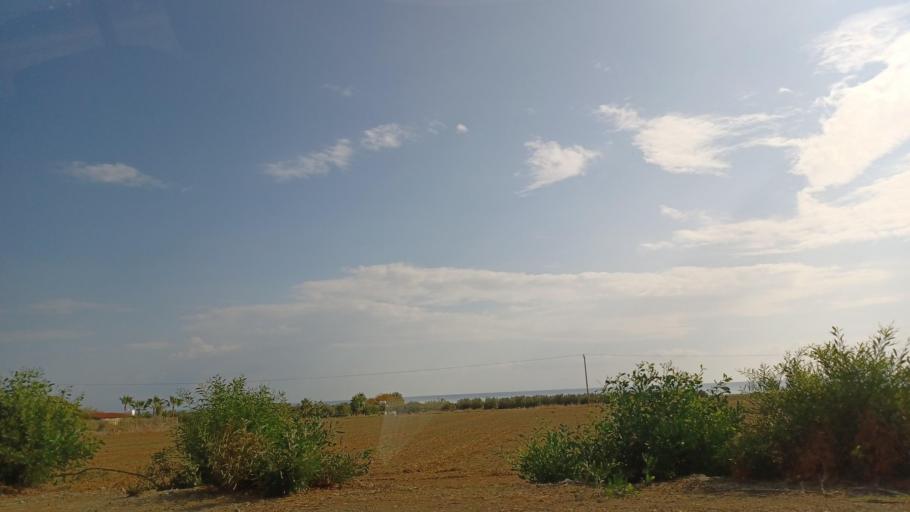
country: CY
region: Larnaka
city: Tersefanou
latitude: 34.8071
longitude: 33.5281
